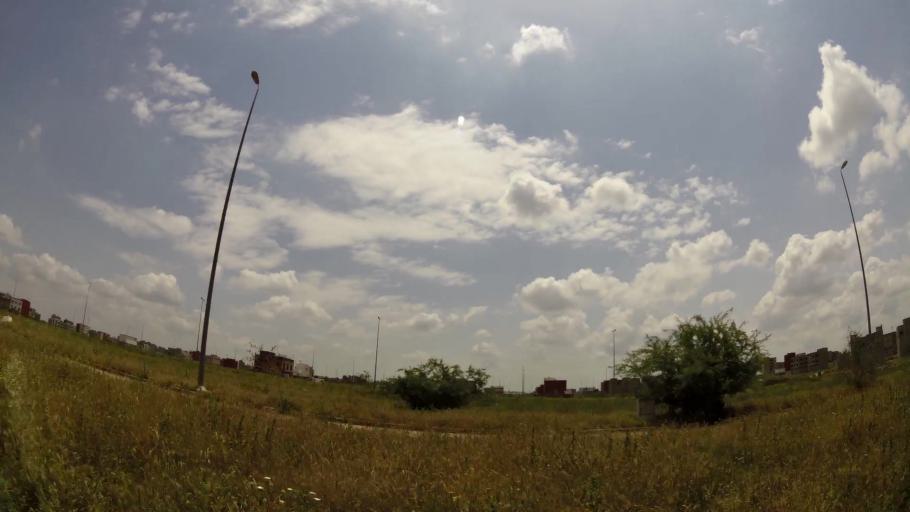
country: MA
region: Rabat-Sale-Zemmour-Zaer
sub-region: Khemisset
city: Tiflet
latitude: 34.0027
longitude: -6.5403
